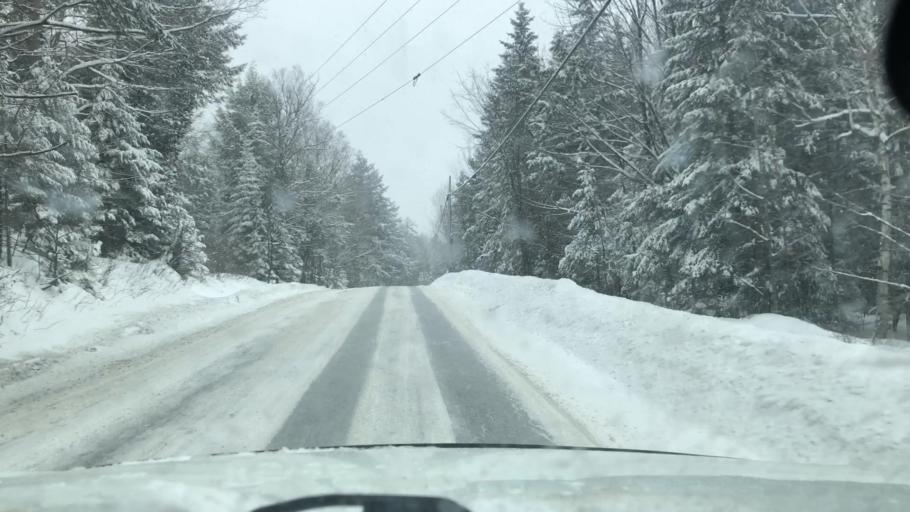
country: CA
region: Quebec
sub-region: Outaouais
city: Gatineau
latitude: 45.5166
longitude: -75.8437
